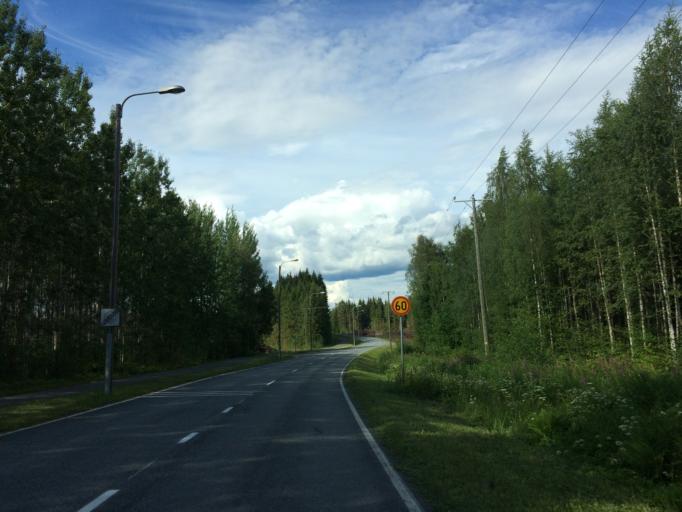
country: FI
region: Haeme
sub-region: Haemeenlinna
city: Janakkala
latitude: 60.9111
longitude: 24.6114
